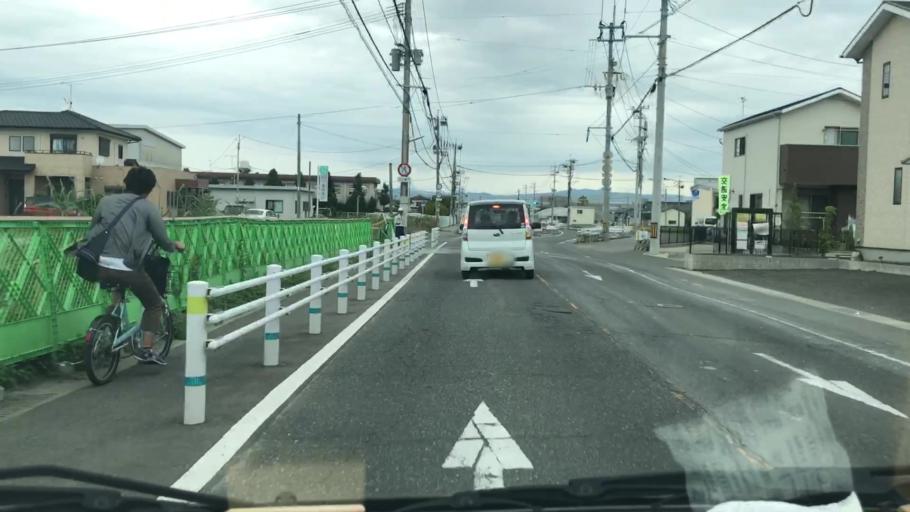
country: JP
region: Saga Prefecture
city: Saga-shi
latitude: 33.2306
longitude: 130.2938
